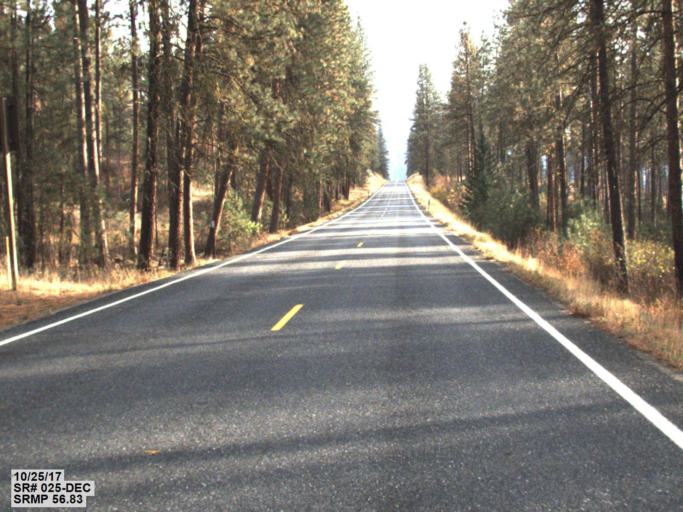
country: US
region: Washington
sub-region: Stevens County
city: Kettle Falls
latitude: 48.2951
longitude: -118.1440
